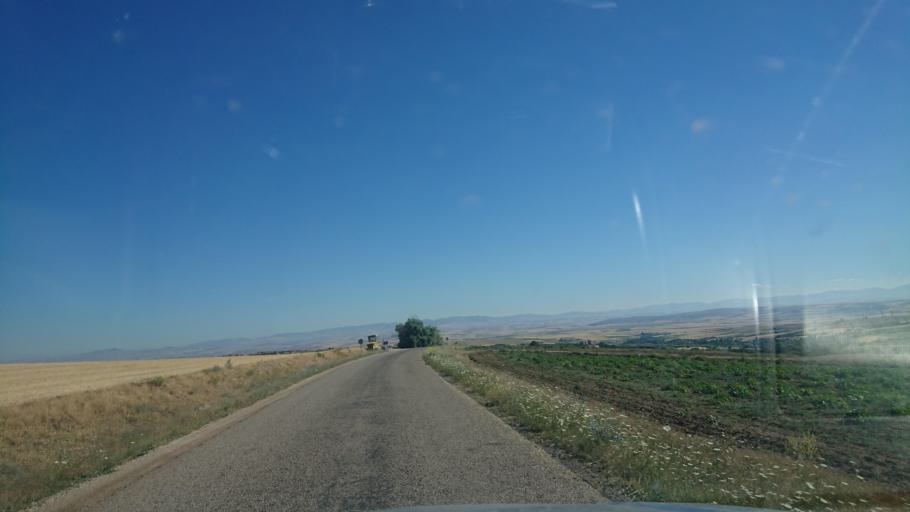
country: TR
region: Aksaray
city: Agacoren
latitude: 38.8473
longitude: 33.9495
